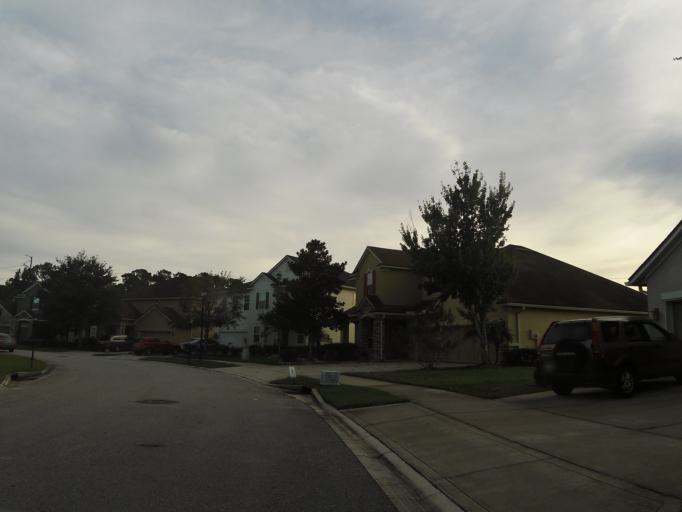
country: US
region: Florida
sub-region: Saint Johns County
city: Fruit Cove
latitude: 30.1489
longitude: -81.5403
